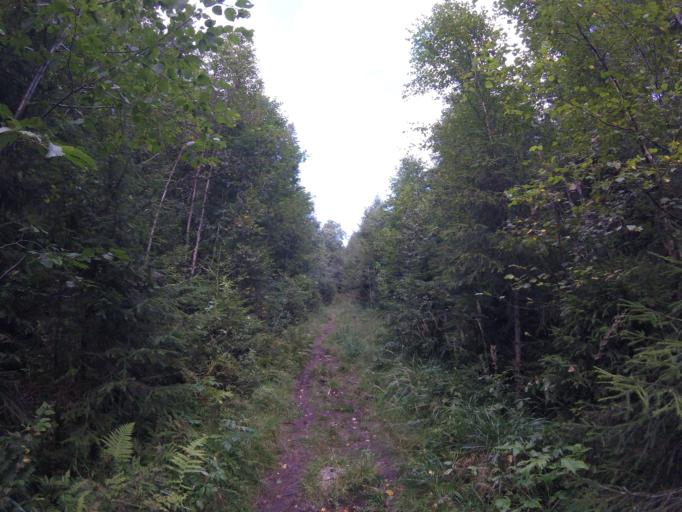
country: NO
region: Akershus
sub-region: Raelingen
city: Fjerdingby
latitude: 59.9175
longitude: 11.0327
